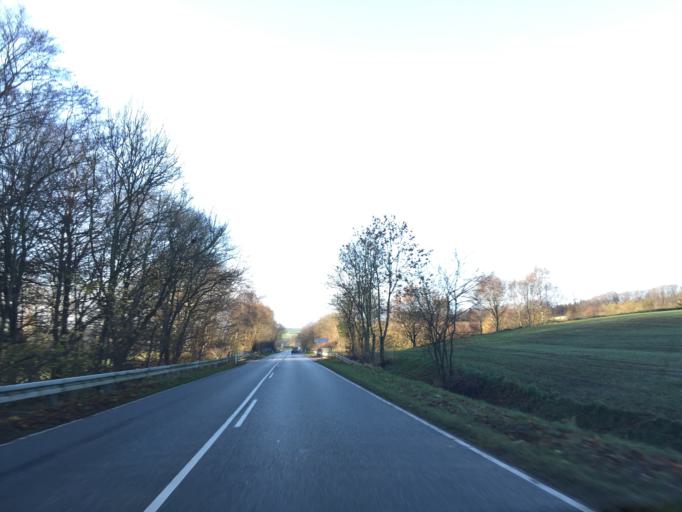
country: DK
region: Central Jutland
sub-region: Skanderborg Kommune
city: Galten
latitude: 56.1748
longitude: 9.8489
